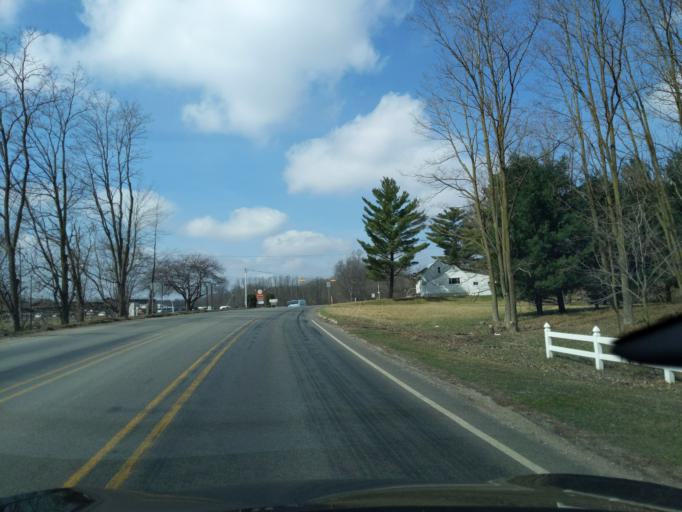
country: US
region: Michigan
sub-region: Calhoun County
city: Marshall
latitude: 42.3486
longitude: -84.9946
